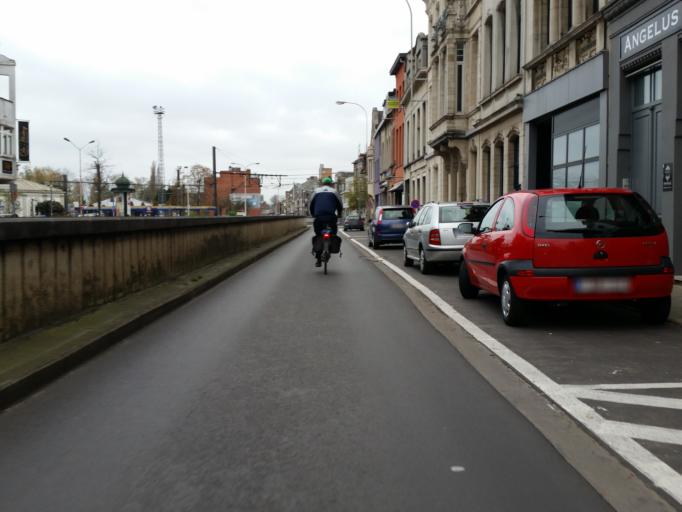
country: BE
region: Flanders
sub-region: Provincie Antwerpen
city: Lier
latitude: 51.1355
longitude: 4.5641
